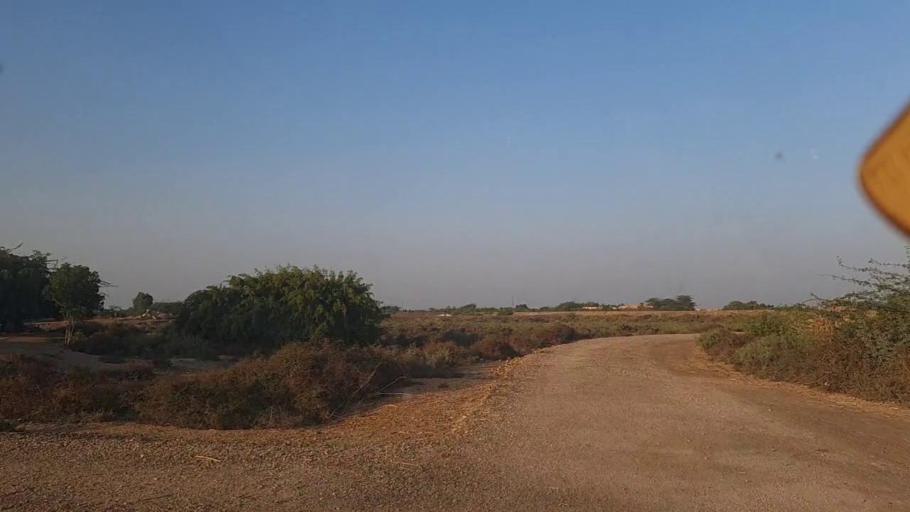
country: PK
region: Sindh
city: Thatta
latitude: 24.6830
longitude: 67.9507
